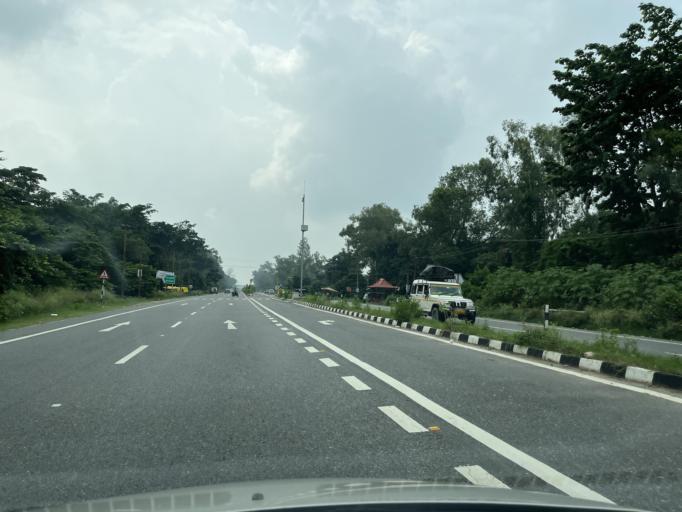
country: IN
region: Uttarakhand
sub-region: Dehradun
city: Doiwala
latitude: 30.1126
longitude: 78.1691
